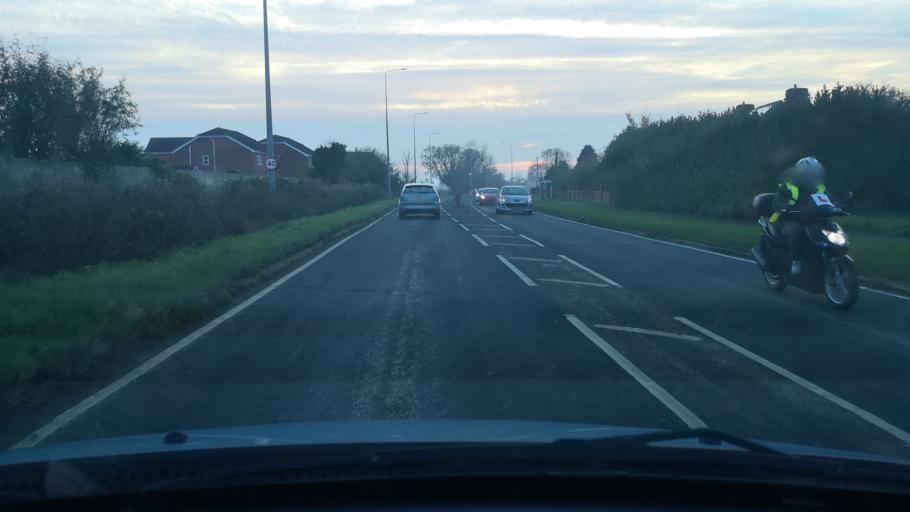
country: GB
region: England
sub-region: North Lincolnshire
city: Gunness
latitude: 53.5793
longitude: -0.7433
